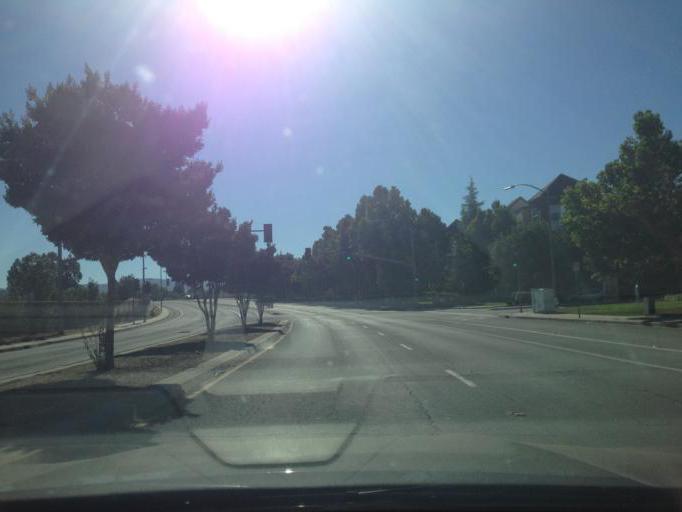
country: US
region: California
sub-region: Santa Clara County
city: Seven Trees
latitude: 37.2433
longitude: -121.8701
